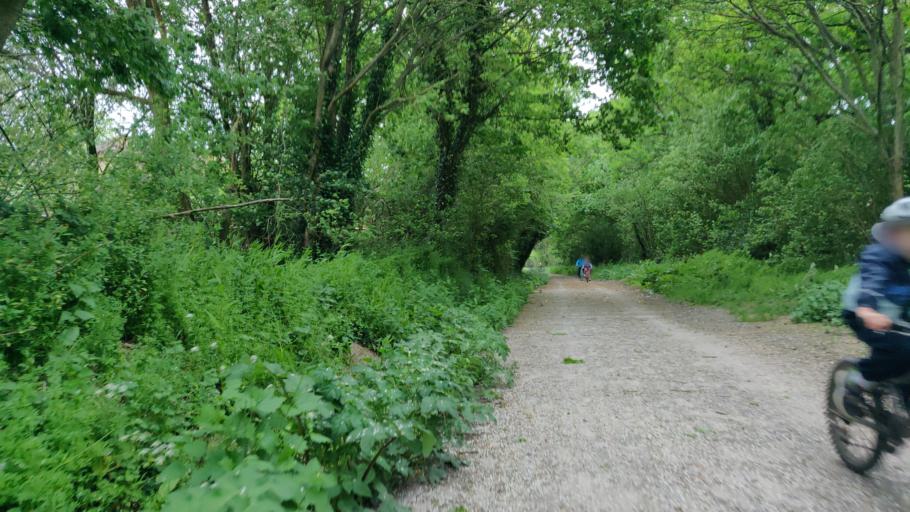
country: GB
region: England
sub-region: West Sussex
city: Partridge Green
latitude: 50.9612
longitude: -0.3117
